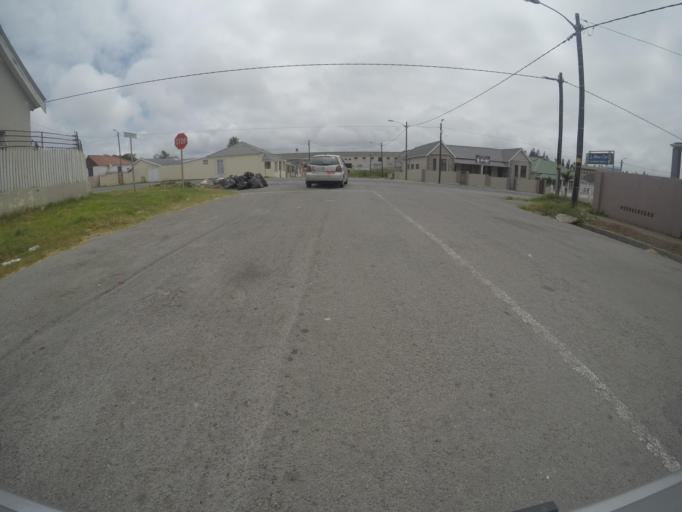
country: ZA
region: Eastern Cape
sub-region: Buffalo City Metropolitan Municipality
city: East London
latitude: -33.0130
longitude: 27.9166
